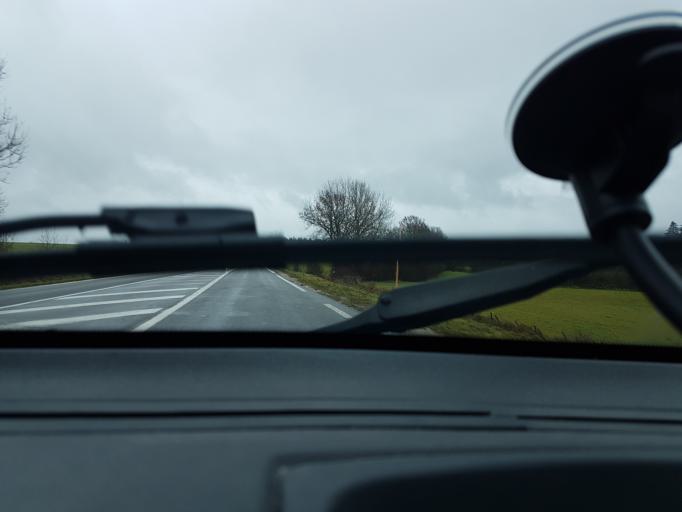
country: FR
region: Franche-Comte
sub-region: Departement du Doubs
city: Valdahon
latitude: 47.1397
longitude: 6.3825
